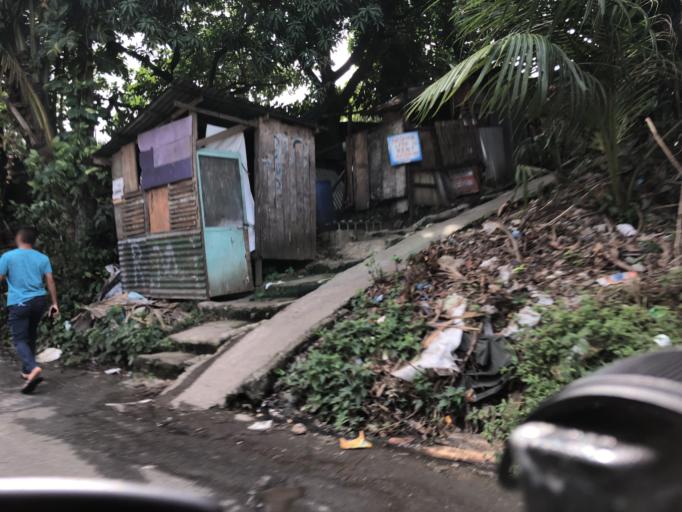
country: PH
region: Central Luzon
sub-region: Province of Bulacan
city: San Jose del Monte
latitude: 14.7579
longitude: 121.0551
